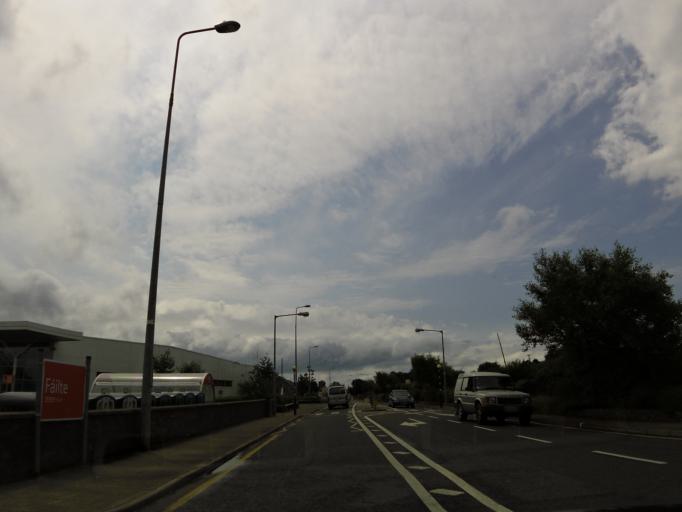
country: IE
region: Munster
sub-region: An Clar
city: Kilrush
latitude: 52.6431
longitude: -9.4766
